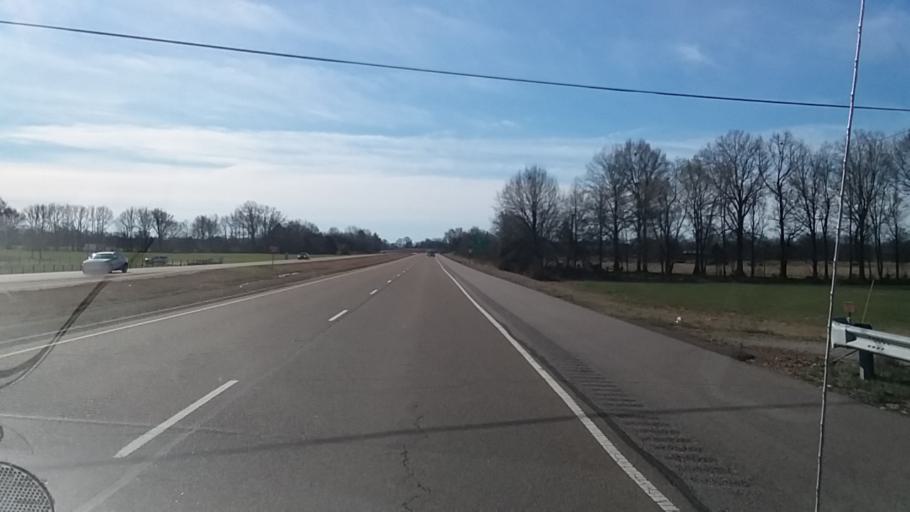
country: US
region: Tennessee
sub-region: Crockett County
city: Alamo
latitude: 35.8450
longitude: -89.1922
